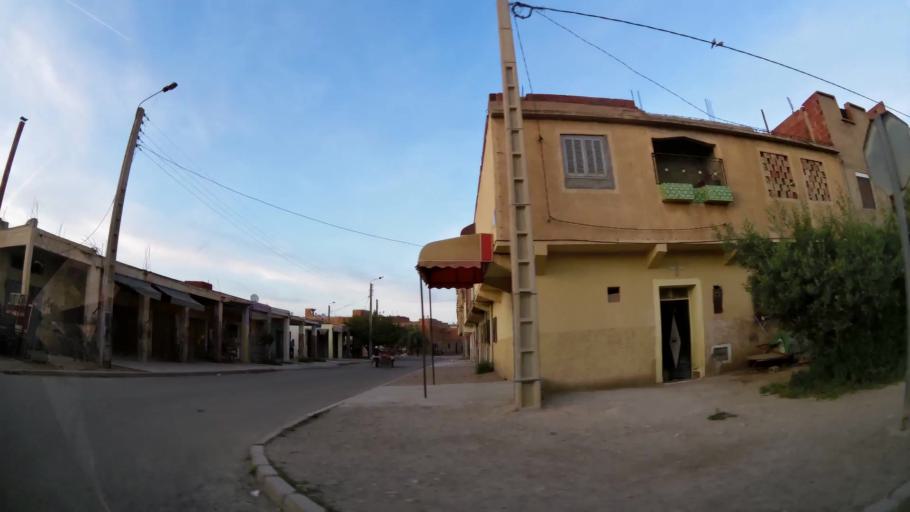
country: MA
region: Oriental
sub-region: Oujda-Angad
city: Oujda
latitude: 34.6823
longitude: -1.8773
